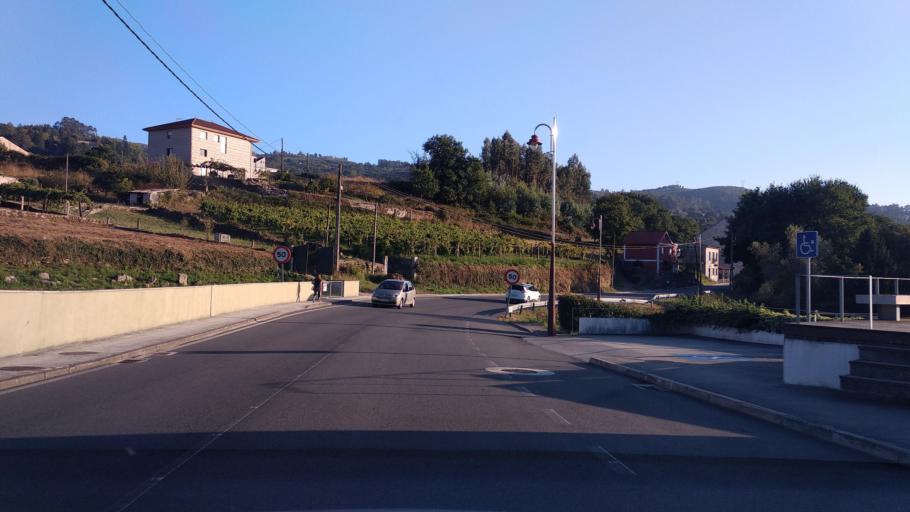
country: ES
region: Galicia
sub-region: Provincia de Pontevedra
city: Redondela
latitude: 42.3367
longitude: -8.5718
